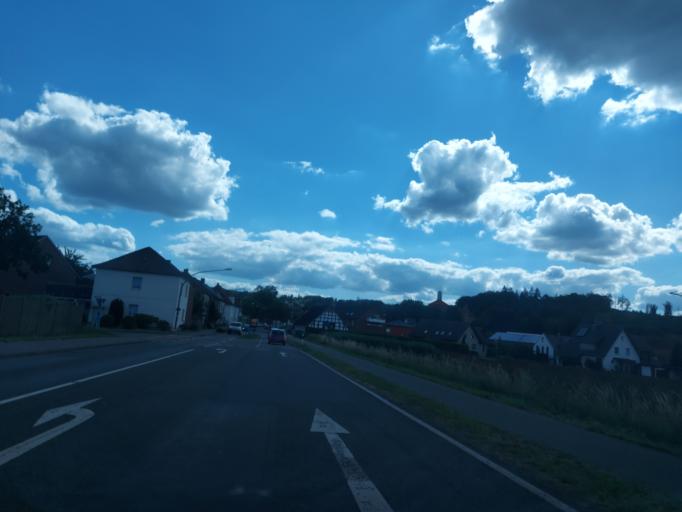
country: DE
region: Lower Saxony
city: Georgsmarienhutte
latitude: 52.2253
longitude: 8.0105
